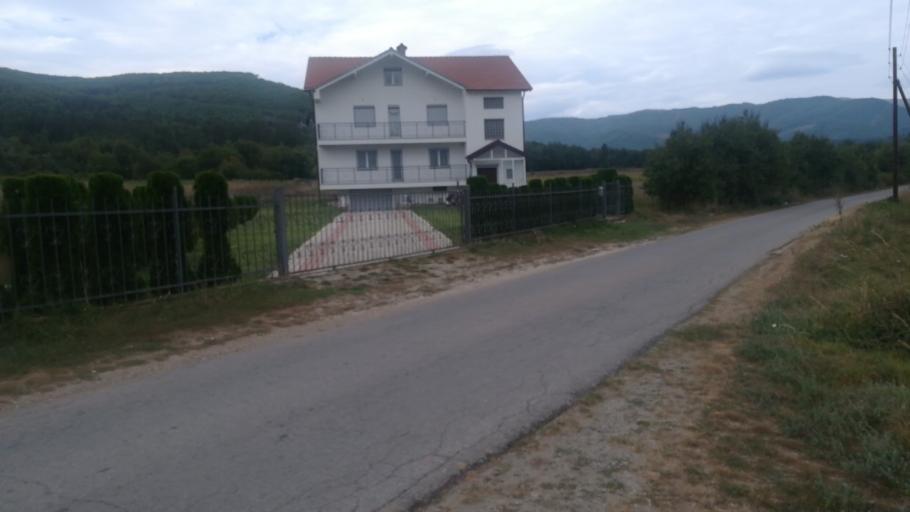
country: MK
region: Debarca
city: Belcista
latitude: 41.2849
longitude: 20.8255
